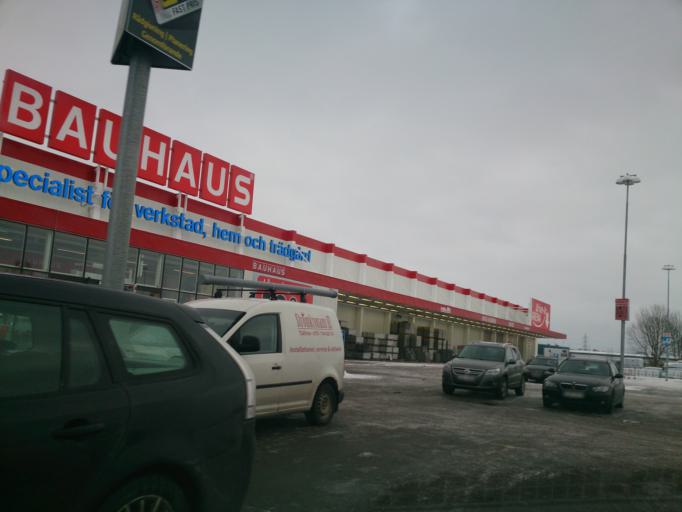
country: SE
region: OEstergoetland
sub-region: Linkopings Kommun
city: Linkoping
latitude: 58.4328
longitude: 15.6081
